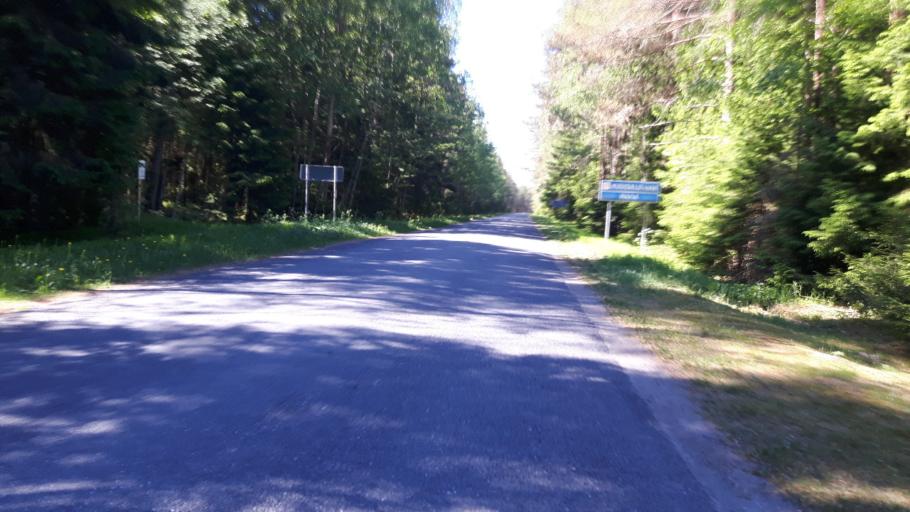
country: EE
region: Harju
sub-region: Loksa linn
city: Loksa
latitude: 59.5701
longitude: 25.7059
